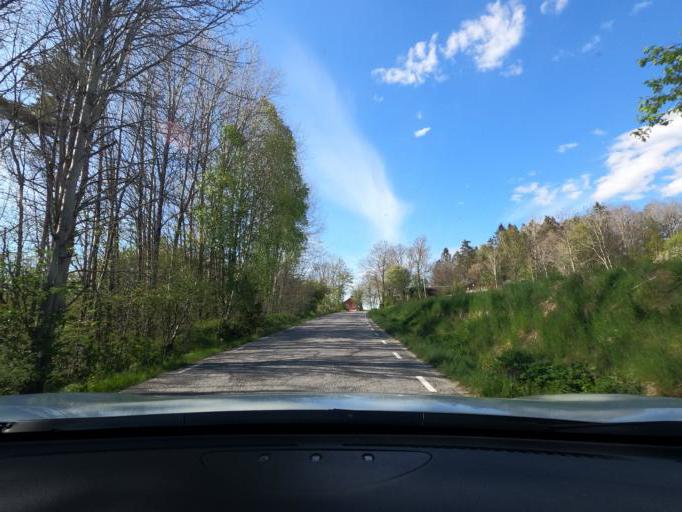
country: SE
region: Vaestra Goetaland
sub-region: Harryda Kommun
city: Ravlanda
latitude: 57.6310
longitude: 12.4985
